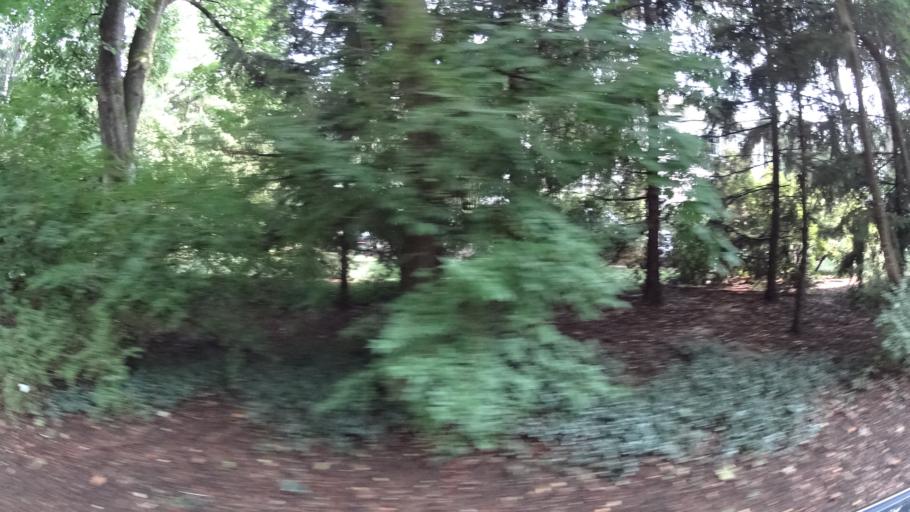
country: US
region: New Jersey
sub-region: Union County
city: Berkeley Heights
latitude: 40.7054
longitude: -74.4298
